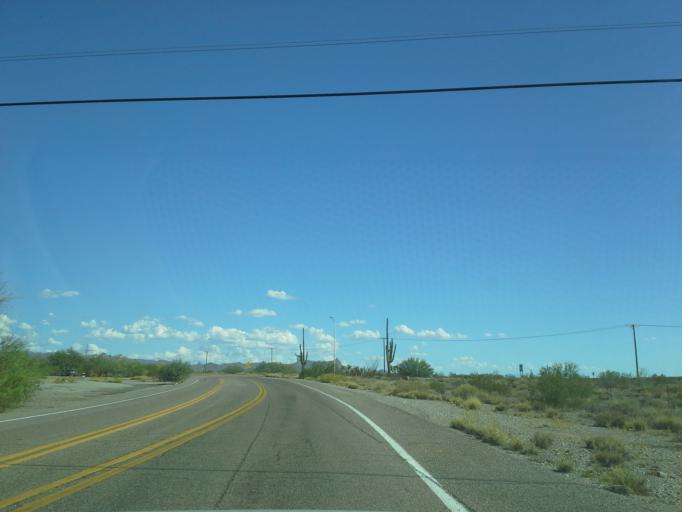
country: US
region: Arizona
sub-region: Pinal County
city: Gold Camp
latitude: 33.2594
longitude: -111.3379
